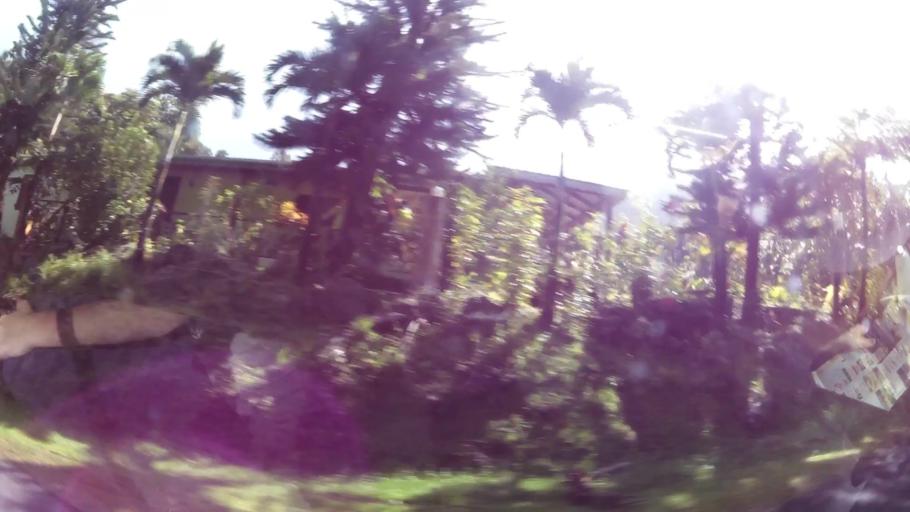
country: DM
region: Saint Paul
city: Pont Casse
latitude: 15.3840
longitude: -61.3376
